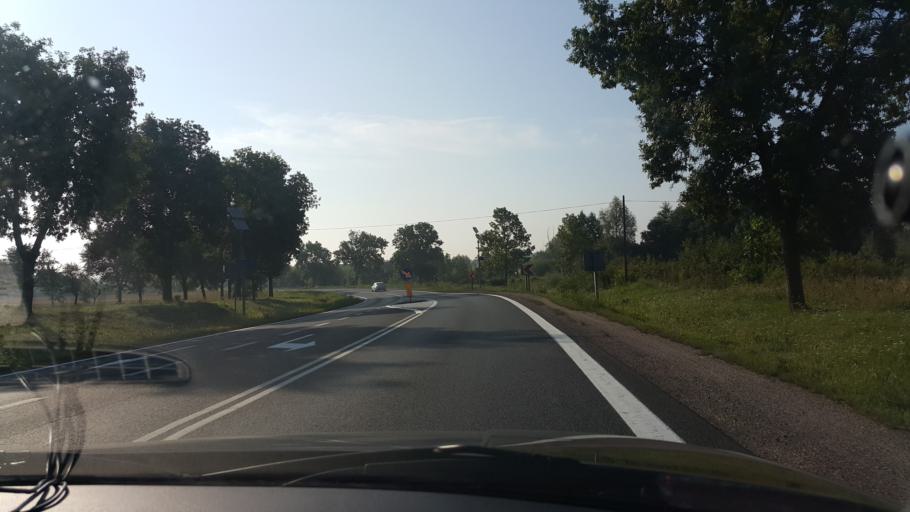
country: PL
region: Masovian Voivodeship
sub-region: Powiat radomski
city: Jedlnia-Letnisko
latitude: 51.3896
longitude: 21.2758
